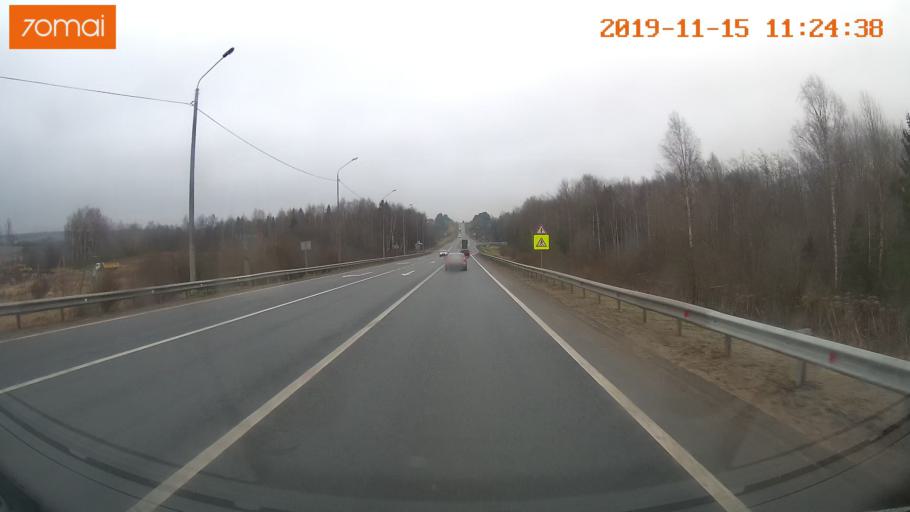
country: RU
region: Vologda
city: Molochnoye
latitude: 59.1581
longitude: 39.4090
